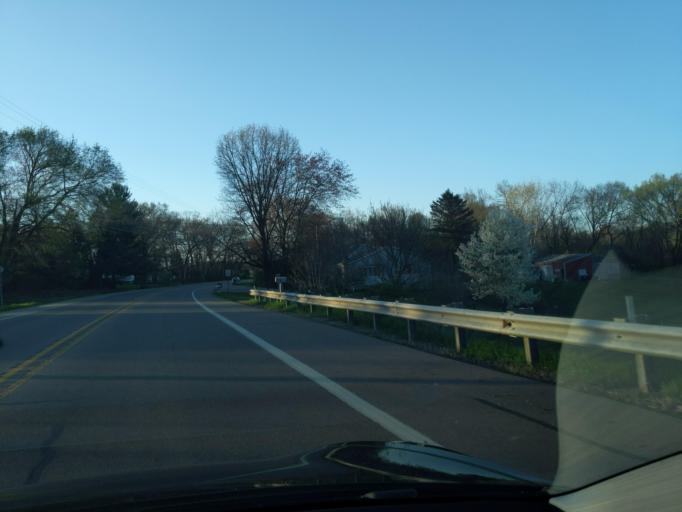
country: US
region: Michigan
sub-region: Ingham County
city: Stockbridge
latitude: 42.4237
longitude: -84.1729
